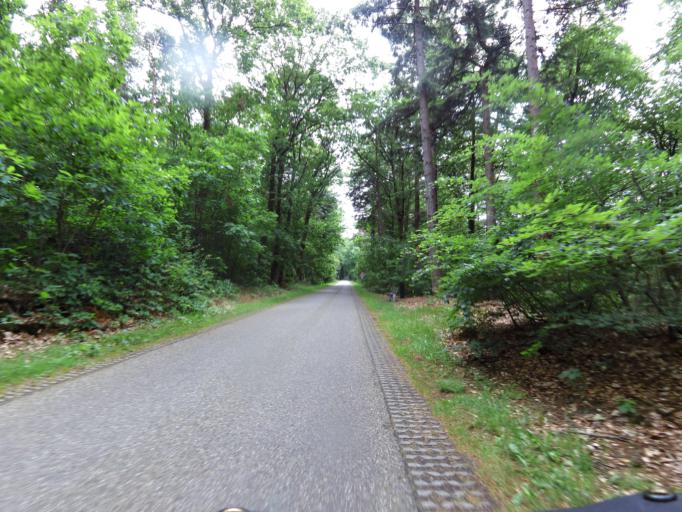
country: NL
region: Gelderland
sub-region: Gemeente Apeldoorn
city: Uddel
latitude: 52.2860
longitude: 5.7972
